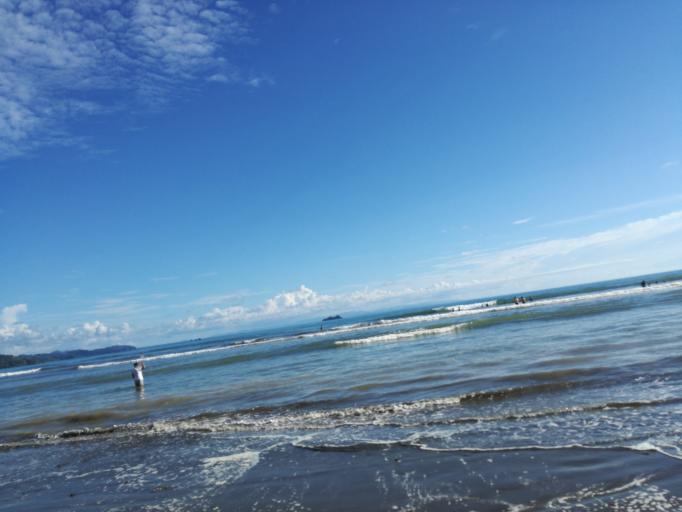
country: CR
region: San Jose
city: Daniel Flores
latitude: 9.1539
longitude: -83.7501
